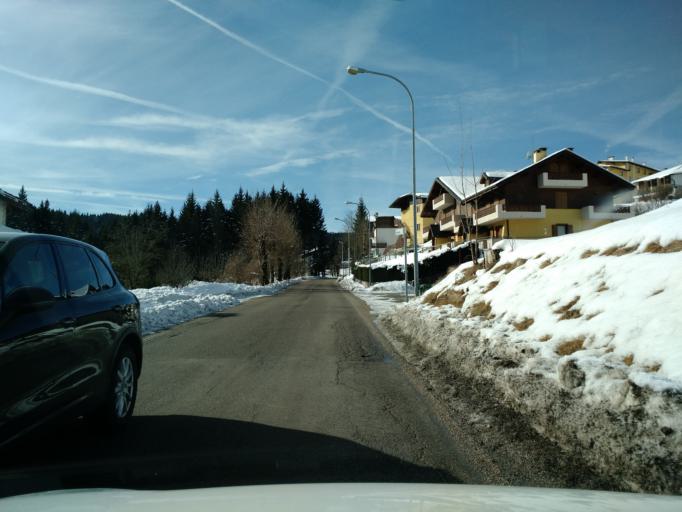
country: IT
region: Veneto
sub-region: Provincia di Vicenza
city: Canove di Roana
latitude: 45.8402
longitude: 11.4641
